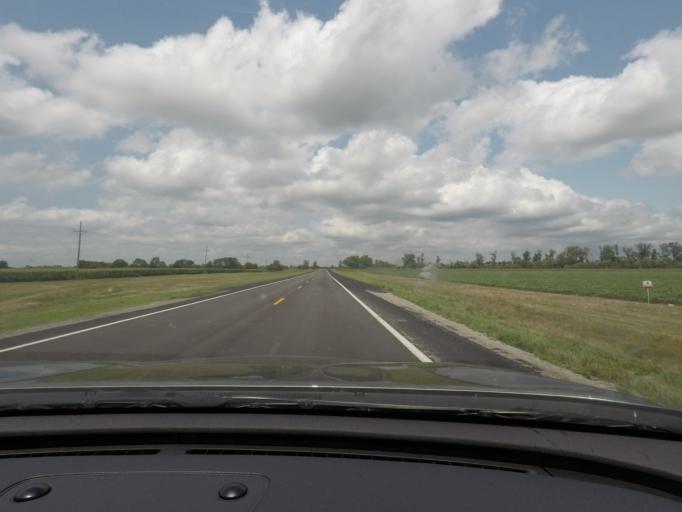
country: US
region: Missouri
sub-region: Carroll County
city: Carrollton
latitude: 39.2715
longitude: -93.5122
